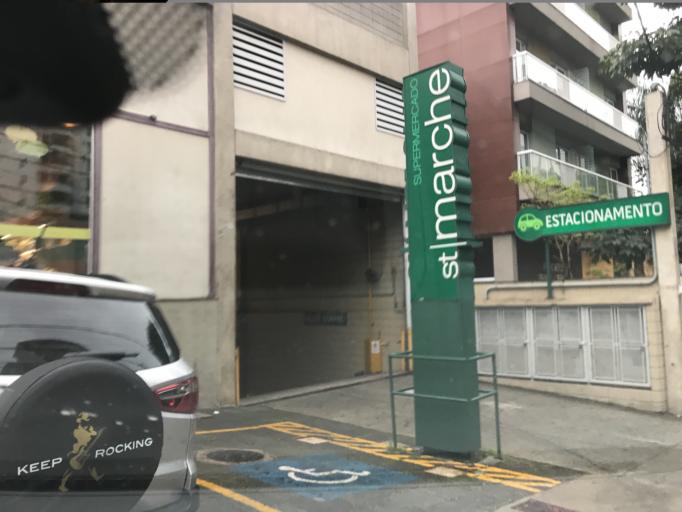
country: BR
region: Sao Paulo
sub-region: Sao Paulo
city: Sao Paulo
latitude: -23.5351
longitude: -46.6871
